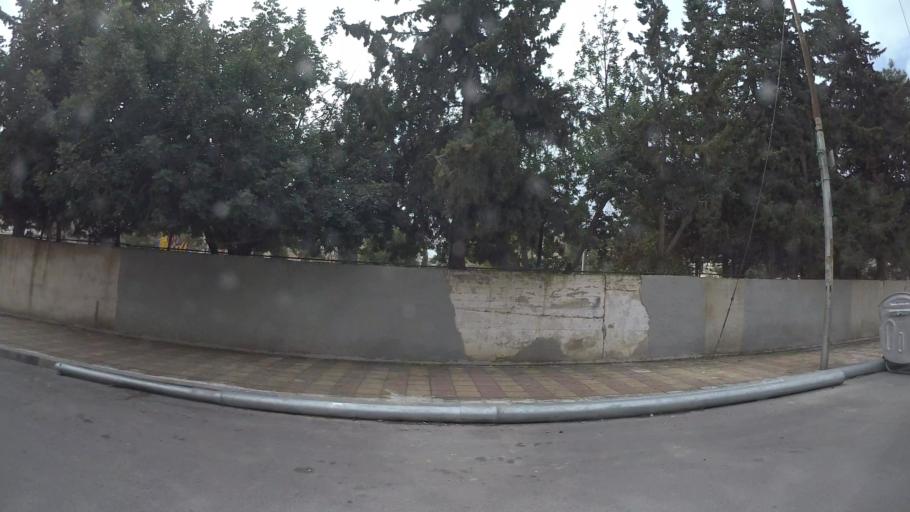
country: JO
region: Amman
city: Amman
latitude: 31.9630
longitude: 35.9512
